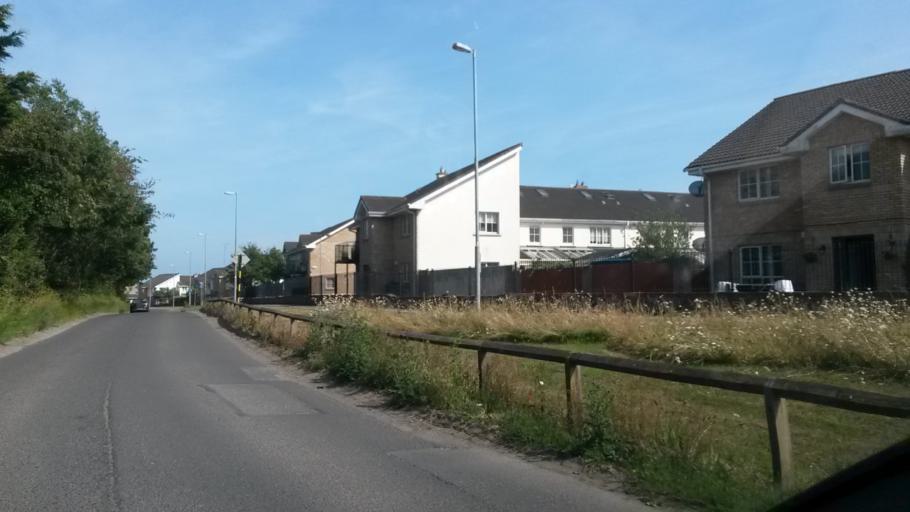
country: IE
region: Leinster
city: Lusk
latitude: 53.5276
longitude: -6.1796
